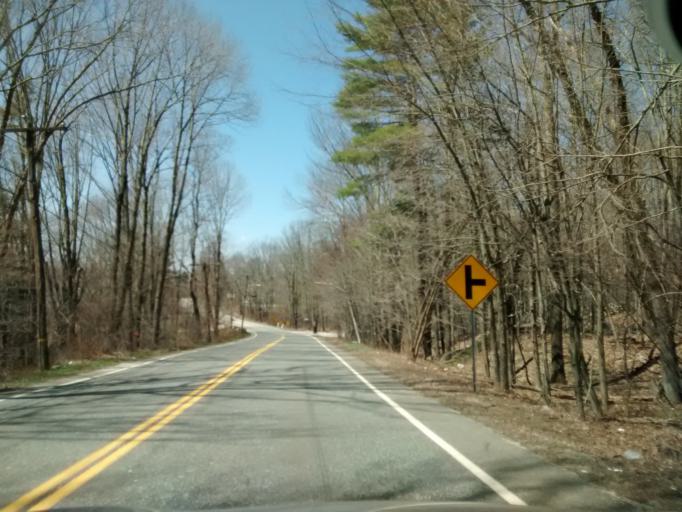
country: US
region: Massachusetts
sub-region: Worcester County
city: Oxford
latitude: 42.1090
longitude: -71.8254
